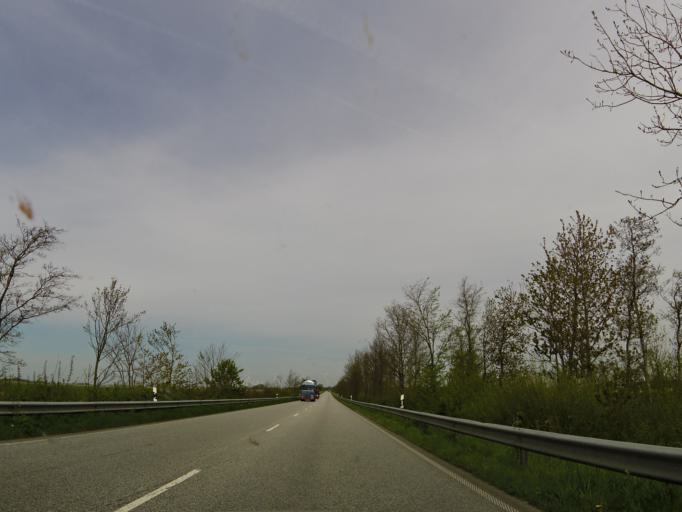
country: DE
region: Schleswig-Holstein
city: Norderwohrden
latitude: 54.2262
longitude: 9.0408
